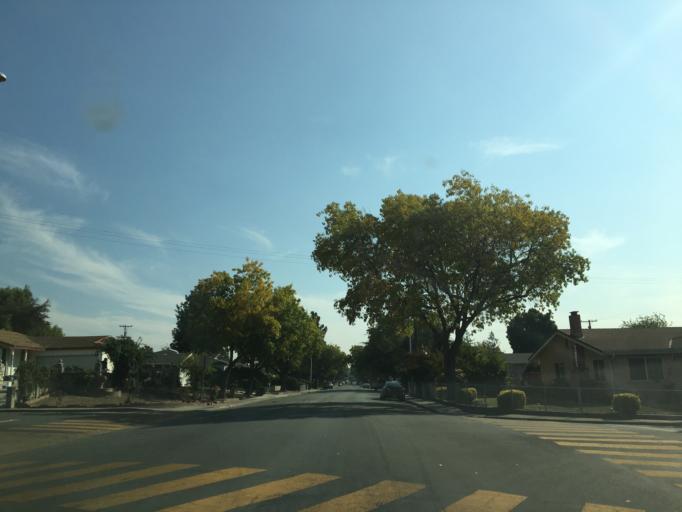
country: US
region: California
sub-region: Santa Clara County
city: Milpitas
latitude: 37.4345
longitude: -121.8750
